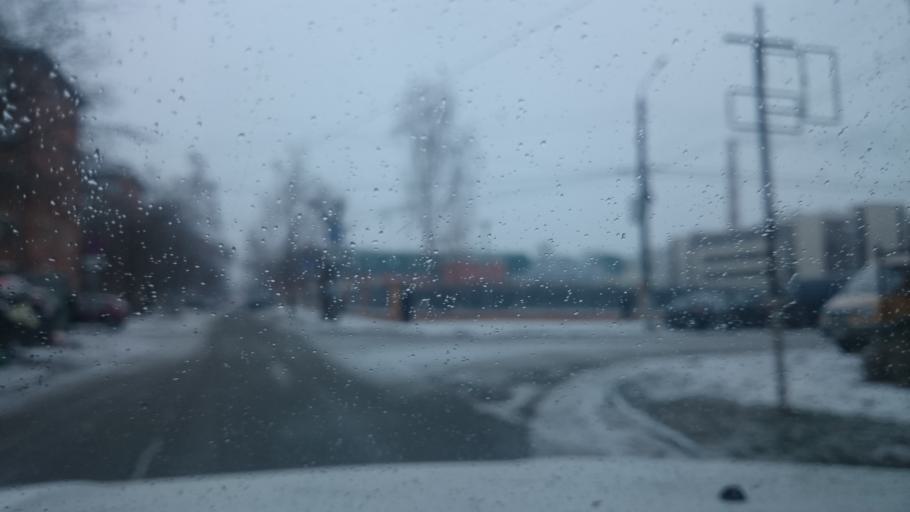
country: RU
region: Tula
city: Tula
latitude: 54.1991
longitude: 37.5964
